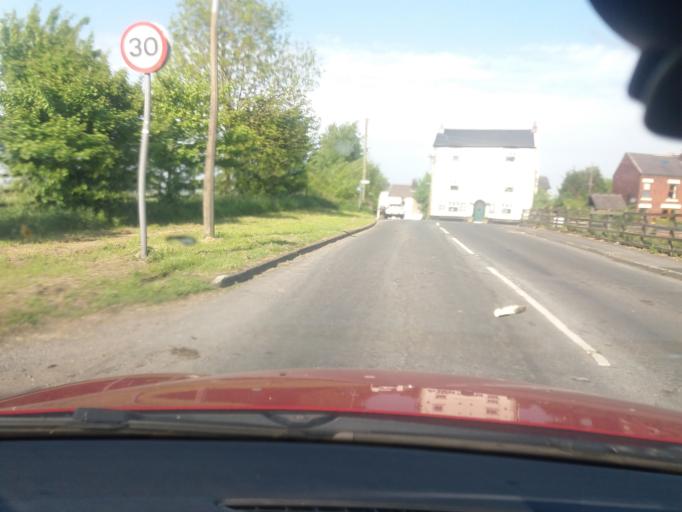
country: GB
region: England
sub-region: Lancashire
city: Adlington
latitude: 53.6259
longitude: -2.5874
